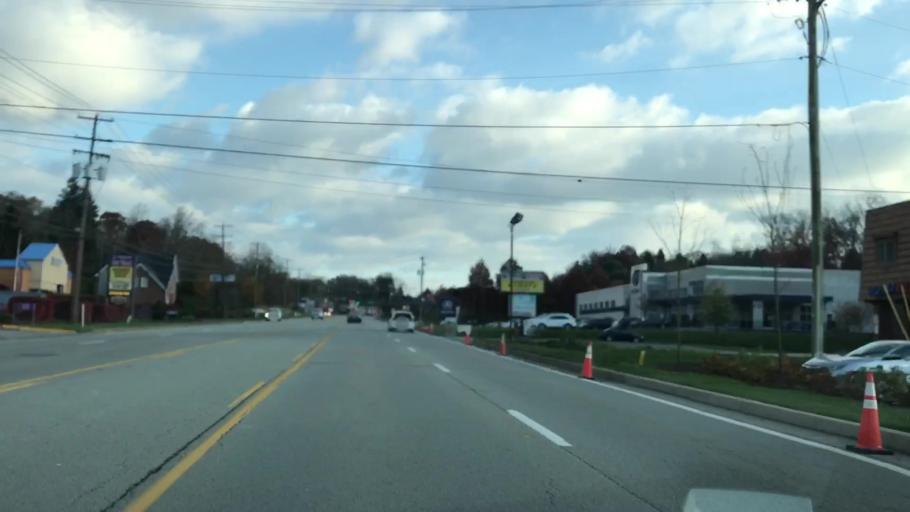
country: US
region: Pennsylvania
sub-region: Washington County
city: Thompsonville
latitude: 40.2802
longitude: -80.1233
